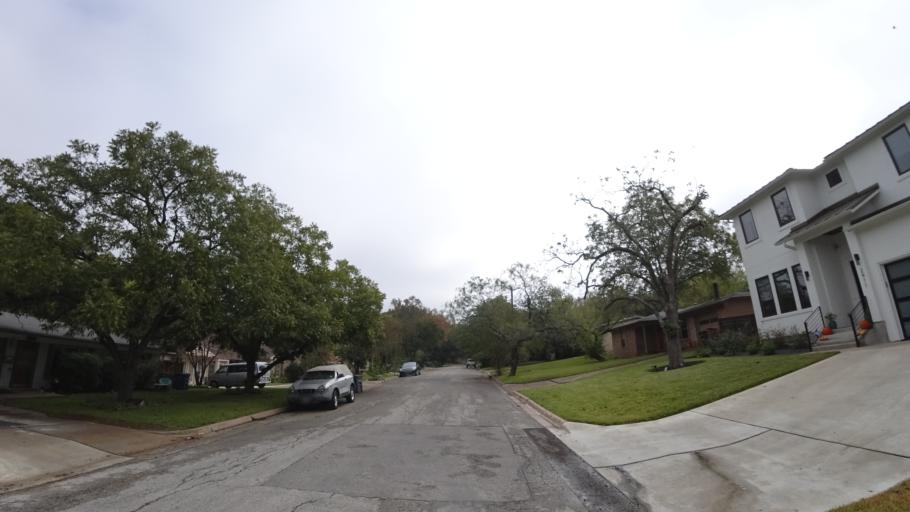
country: US
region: Texas
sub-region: Travis County
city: Rollingwood
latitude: 30.2488
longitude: -97.7835
